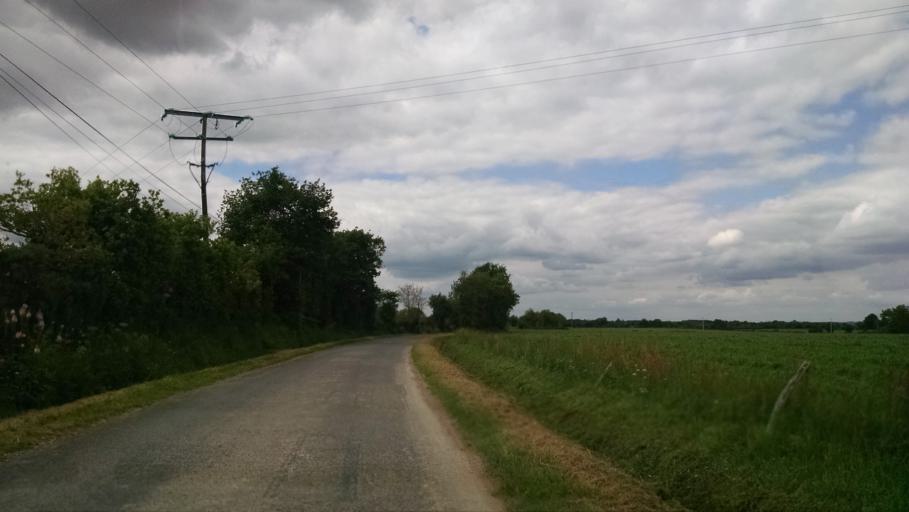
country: FR
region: Pays de la Loire
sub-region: Departement de la Loire-Atlantique
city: Remouille
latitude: 47.0150
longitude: -1.3772
